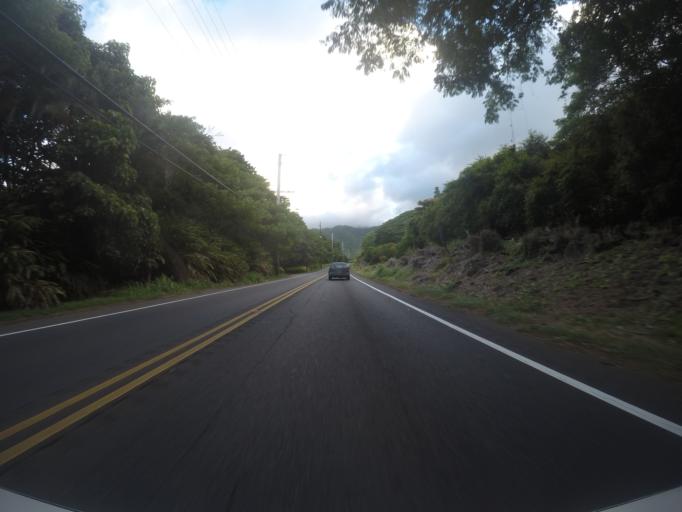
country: US
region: Hawaii
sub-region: Honolulu County
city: Ka'a'awa
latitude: 21.5137
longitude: -157.8467
